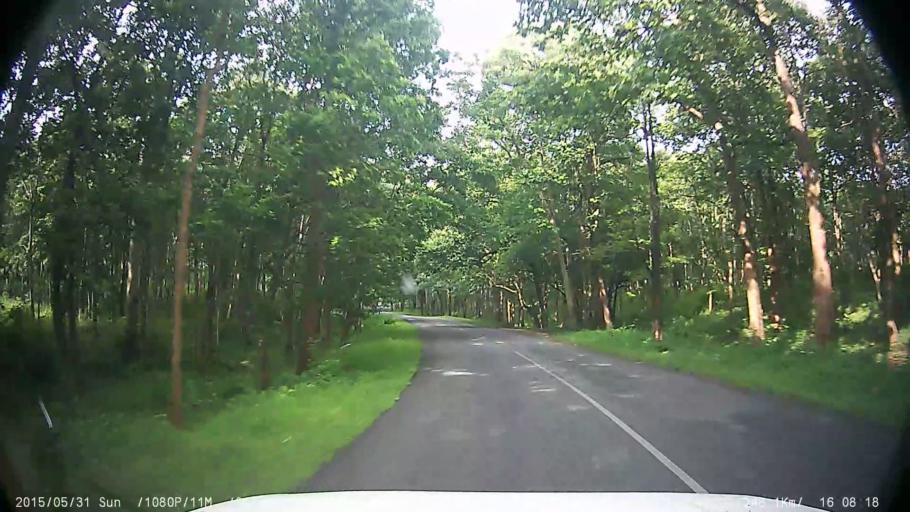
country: IN
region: Karnataka
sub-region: Mysore
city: Sargur
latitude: 11.7231
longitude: 76.4294
